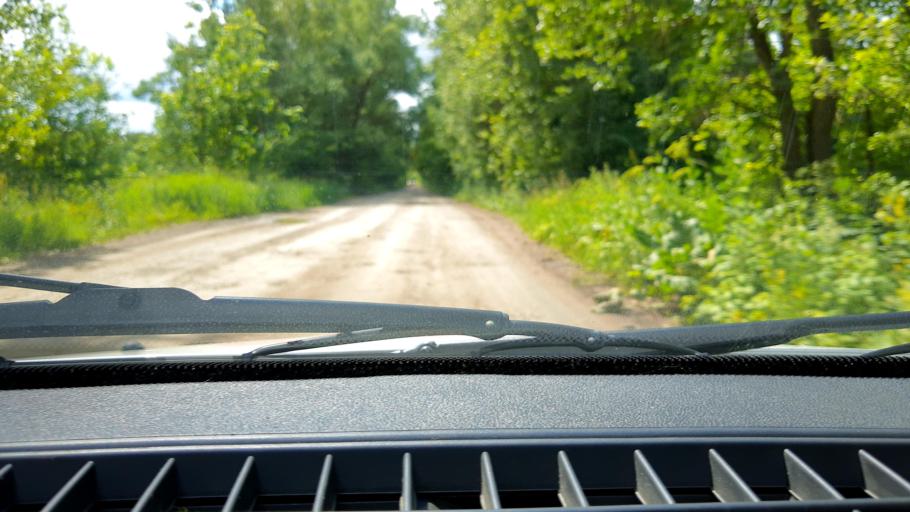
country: RU
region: Bashkortostan
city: Ufa
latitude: 54.6818
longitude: 56.0607
